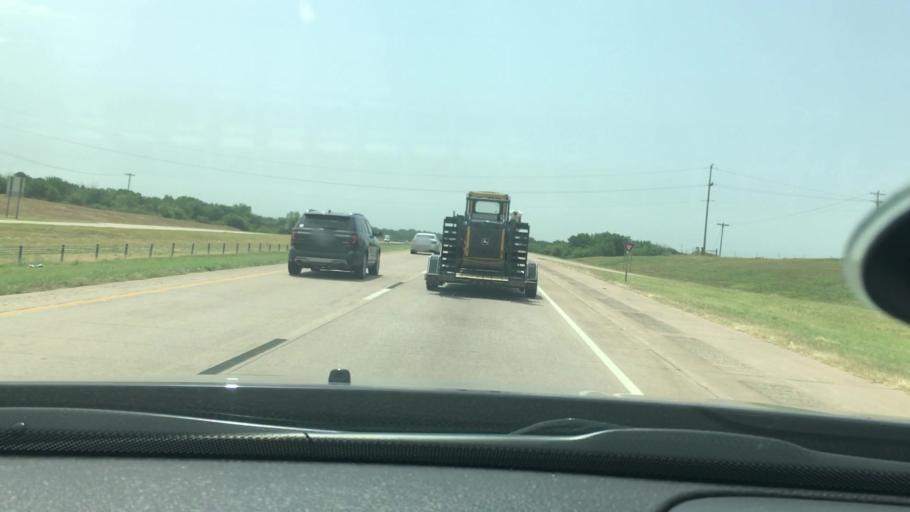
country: US
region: Oklahoma
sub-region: Garvin County
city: Pauls Valley
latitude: 34.7040
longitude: -97.2437
